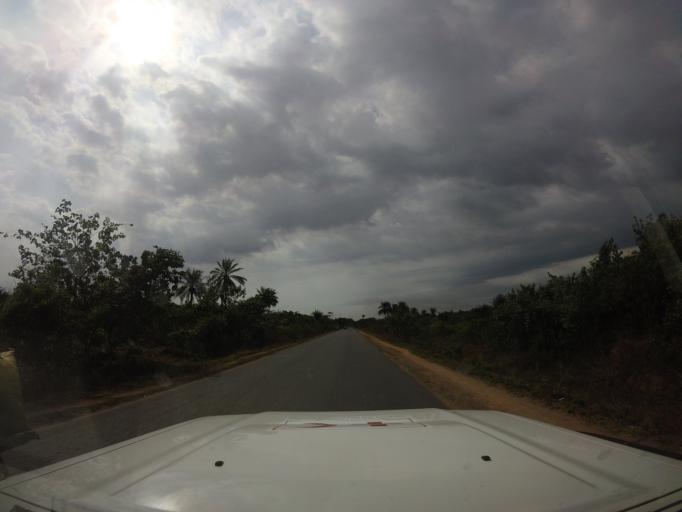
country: LR
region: Montserrado
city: Monrovia
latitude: 6.5018
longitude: -10.8162
